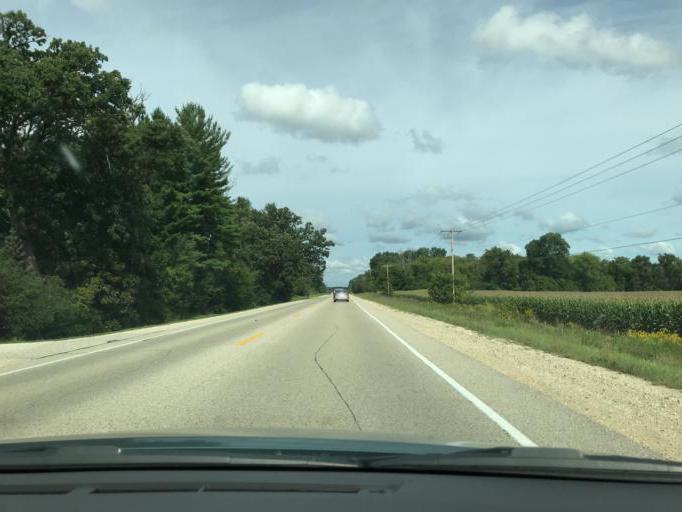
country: US
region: Wisconsin
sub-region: Racine County
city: Bohners Lake
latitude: 42.6194
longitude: -88.2370
